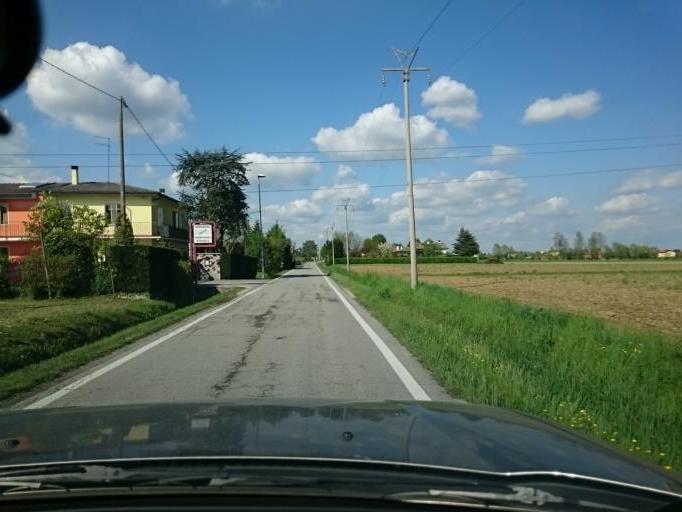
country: IT
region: Veneto
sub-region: Provincia di Padova
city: Pionca
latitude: 45.4645
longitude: 11.9775
